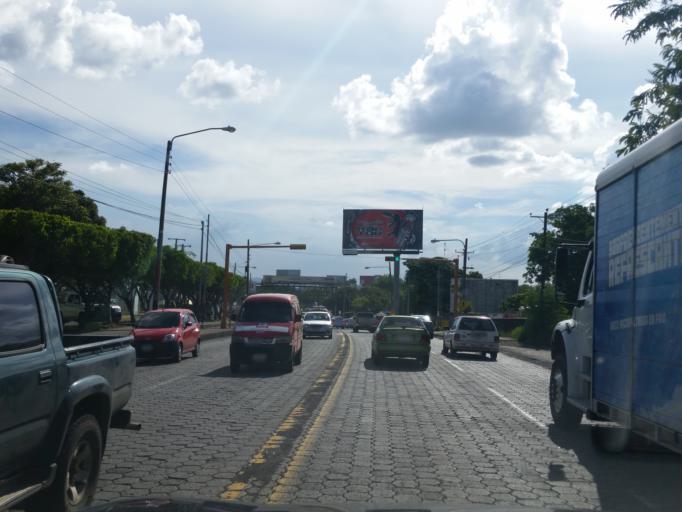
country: NI
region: Managua
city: Managua
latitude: 12.1315
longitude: -86.2605
